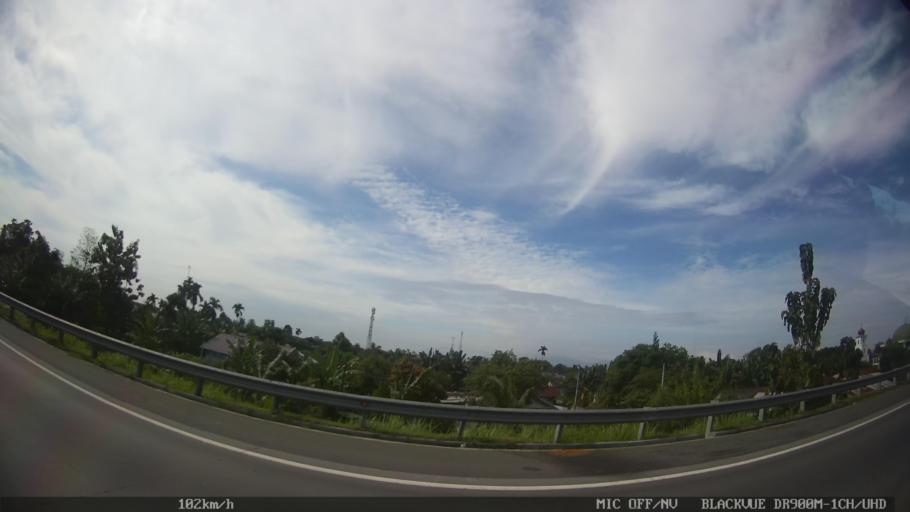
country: ID
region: North Sumatra
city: Sunggal
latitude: 3.6377
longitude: 98.5963
